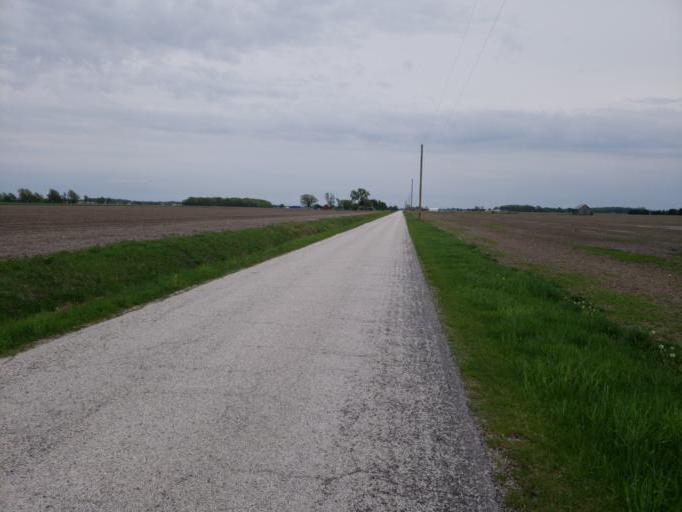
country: US
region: Ohio
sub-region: Wood County
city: Haskins
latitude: 41.4575
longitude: -83.6892
